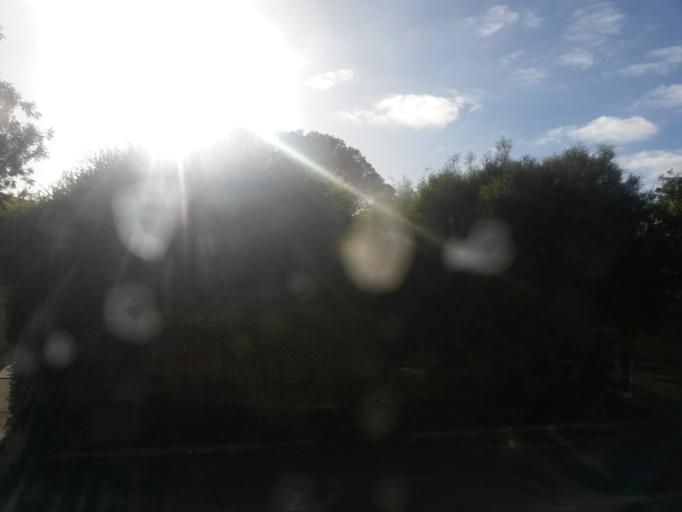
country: AU
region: South Australia
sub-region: Prospect
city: Prospect
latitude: -34.8905
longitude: 138.5764
